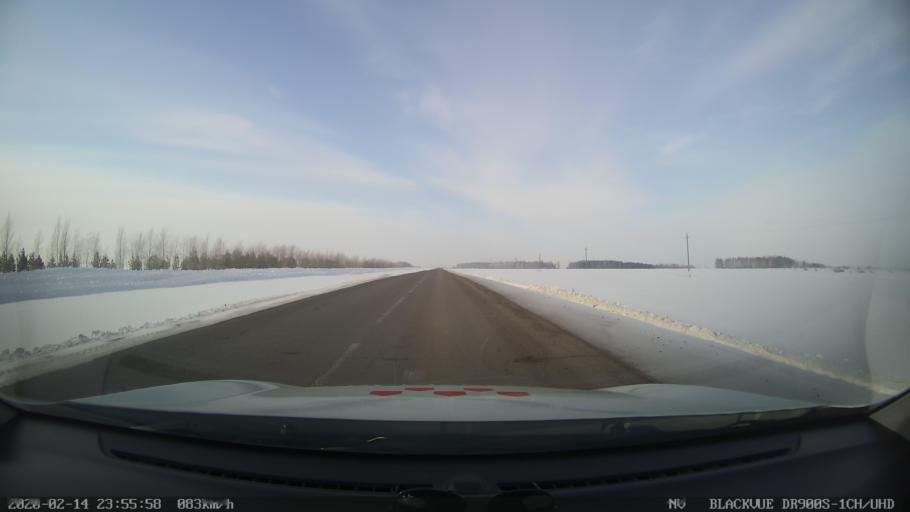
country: RU
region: Tatarstan
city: Kuybyshevskiy Zaton
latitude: 55.3203
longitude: 49.1374
